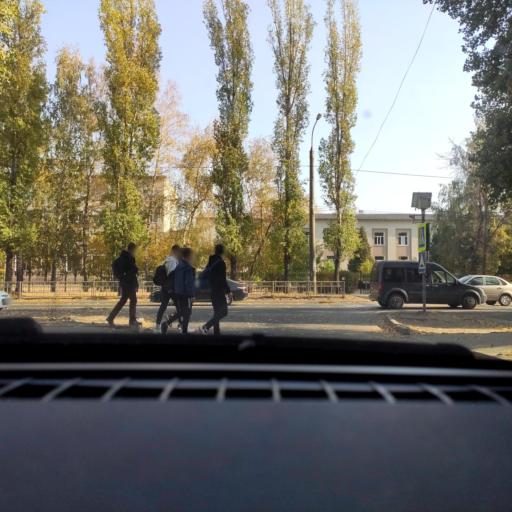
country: RU
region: Voronezj
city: Voronezh
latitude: 51.6471
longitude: 39.2430
